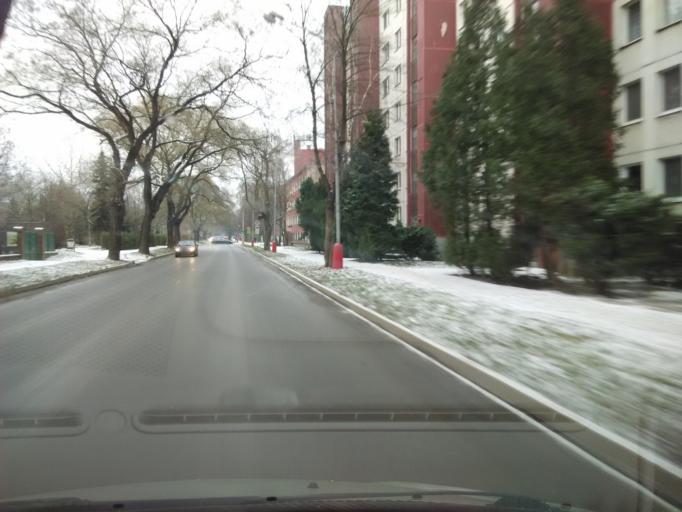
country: SK
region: Nitriansky
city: Zlate Moravce
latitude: 48.3873
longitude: 18.3812
